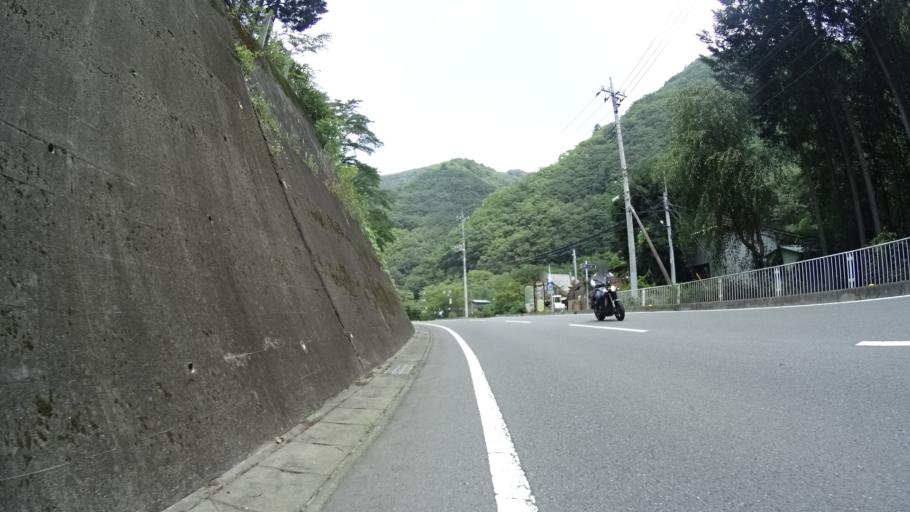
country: JP
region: Gunma
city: Tomioka
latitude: 36.0868
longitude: 138.7270
